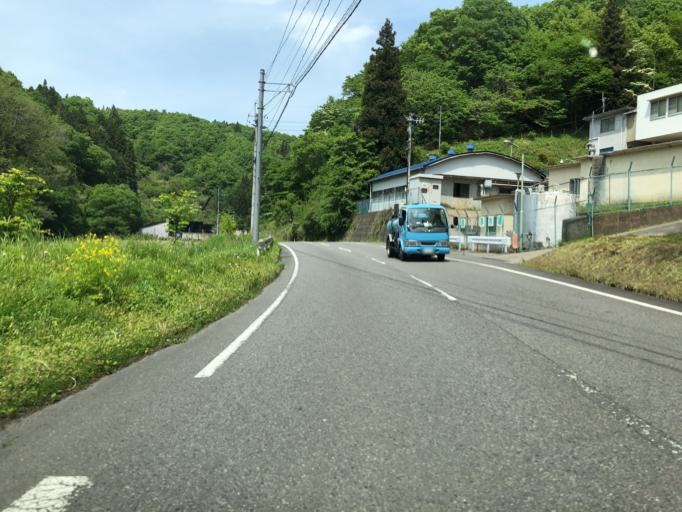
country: JP
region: Fukushima
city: Ishikawa
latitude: 37.1798
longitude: 140.4731
